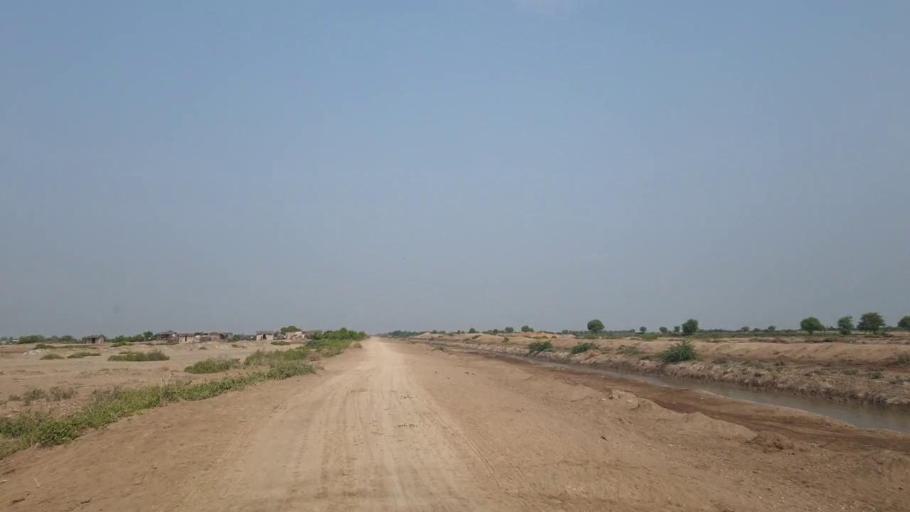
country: PK
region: Sindh
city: Badin
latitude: 24.7260
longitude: 68.7688
